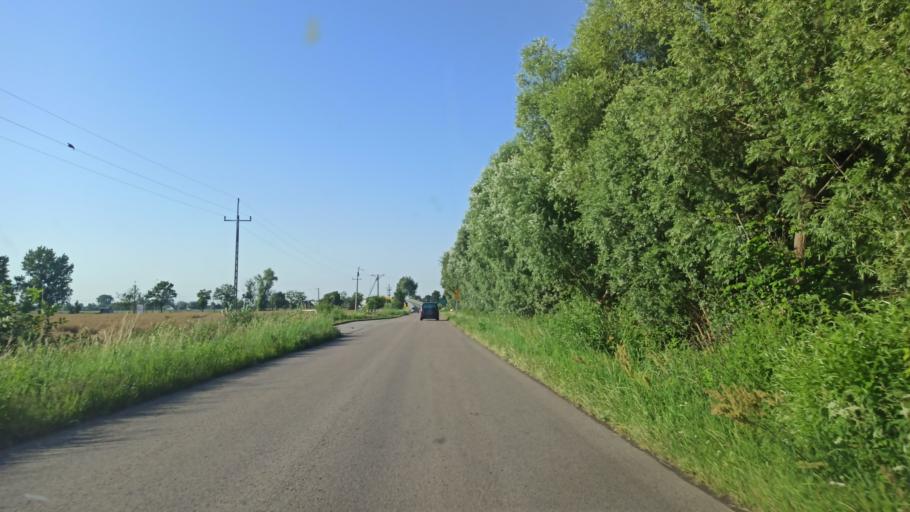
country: PL
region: Warmian-Masurian Voivodeship
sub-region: Powiat elblaski
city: Elblag
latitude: 54.1690
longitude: 19.3305
